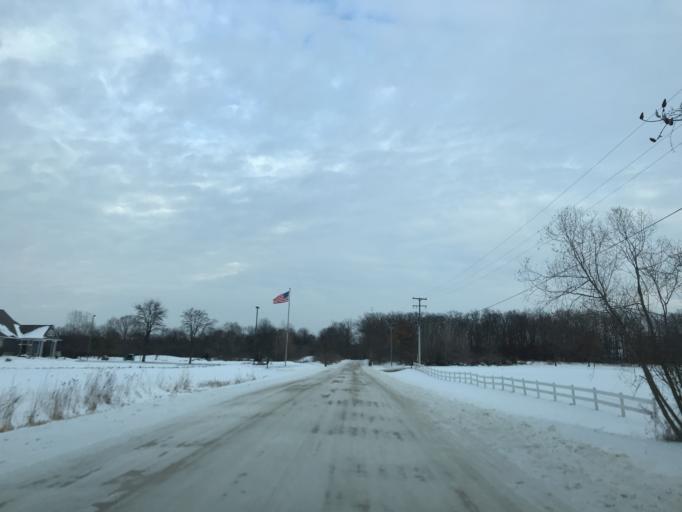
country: US
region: Michigan
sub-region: Livingston County
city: Whitmore Lake
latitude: 42.4015
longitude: -83.7421
